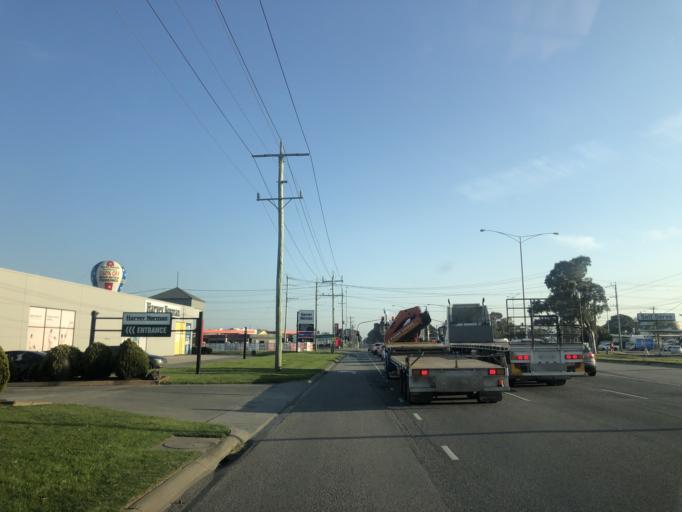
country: AU
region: Victoria
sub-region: Casey
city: Doveton
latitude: -38.0134
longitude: 145.2158
